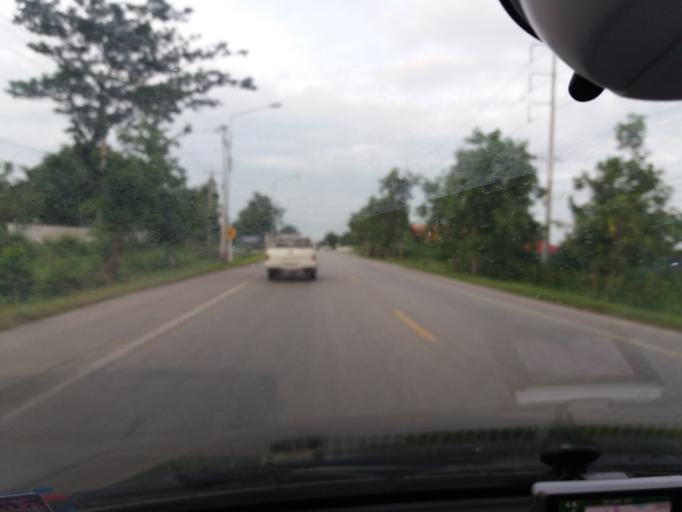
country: TH
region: Suphan Buri
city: U Thong
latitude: 14.4185
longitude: 99.9053
